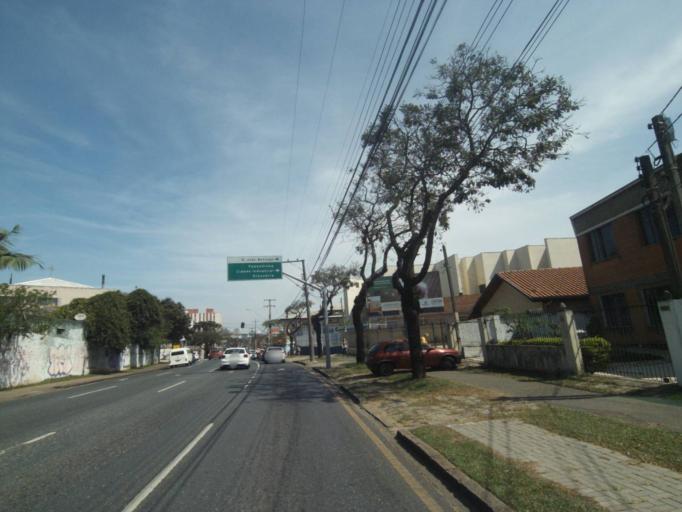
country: BR
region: Parana
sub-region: Curitiba
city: Curitiba
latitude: -25.4739
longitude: -49.2959
